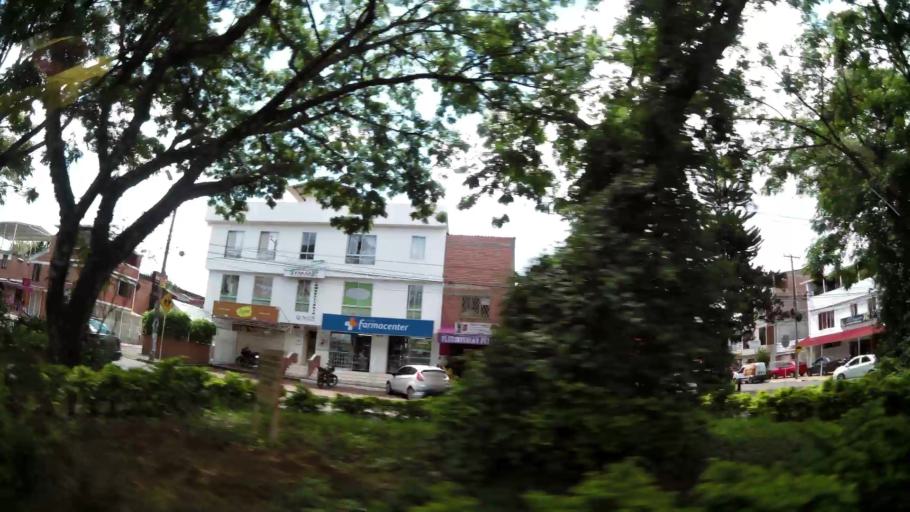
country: CO
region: Valle del Cauca
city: Cali
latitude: 3.3820
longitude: -76.5204
